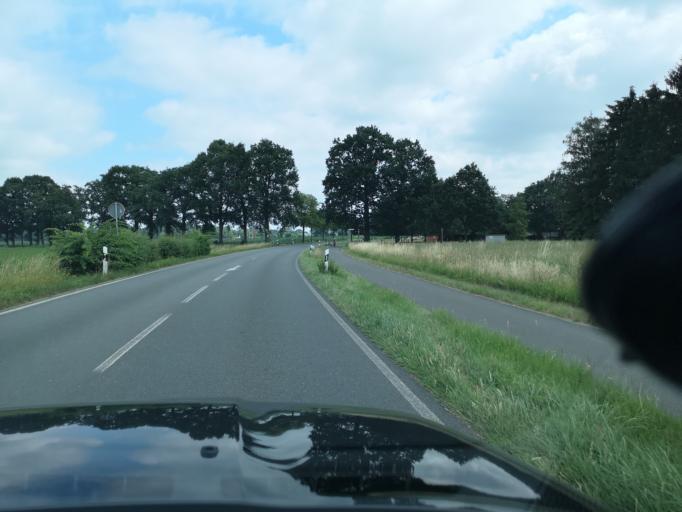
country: DE
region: North Rhine-Westphalia
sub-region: Regierungsbezirk Dusseldorf
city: Wesel
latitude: 51.6864
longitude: 6.6384
